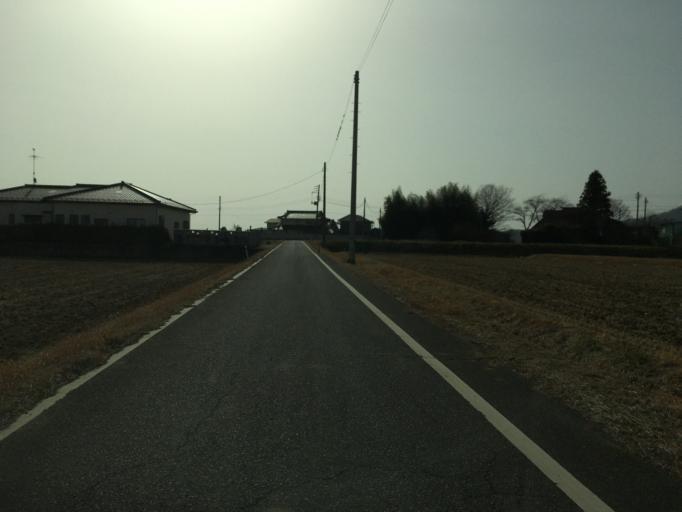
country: JP
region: Fukushima
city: Motomiya
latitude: 37.5342
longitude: 140.3901
